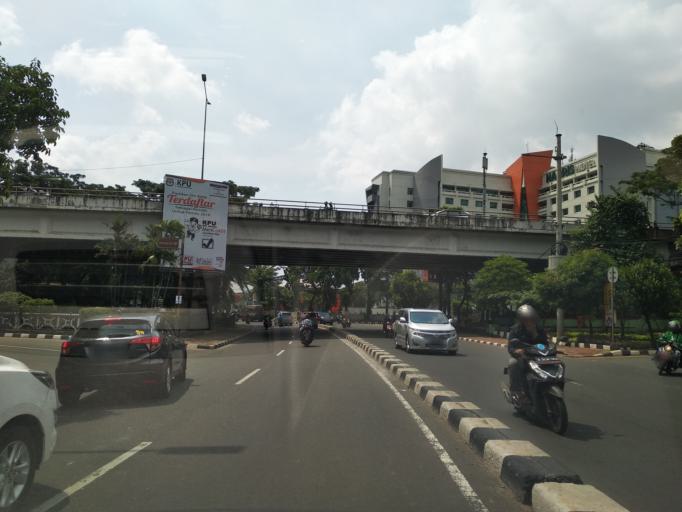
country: ID
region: Jakarta Raya
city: Jakarta
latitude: -6.2240
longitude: 106.8475
